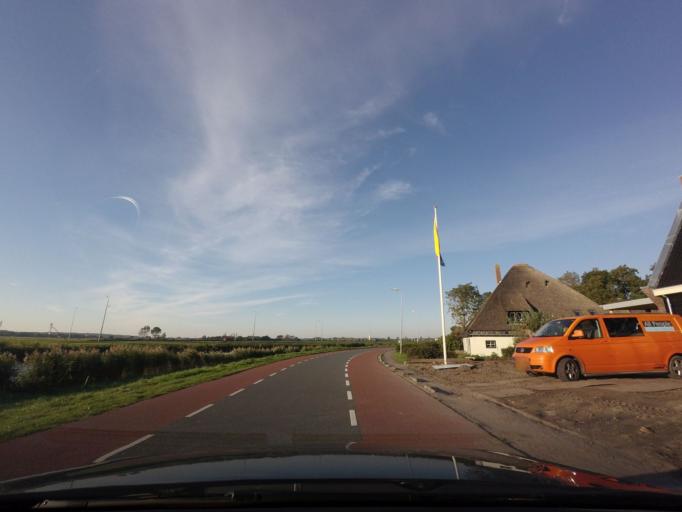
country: NL
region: North Holland
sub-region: Gemeente Alkmaar
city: Alkmaar
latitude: 52.6623
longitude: 4.7460
